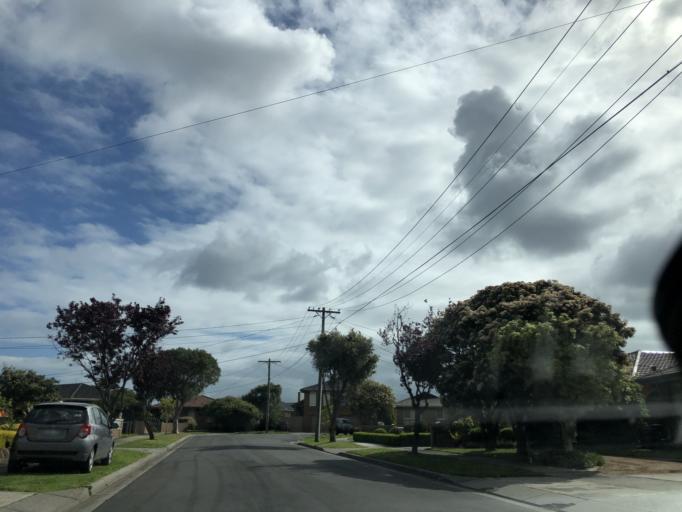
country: AU
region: Victoria
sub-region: Kingston
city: Clayton South
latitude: -37.9387
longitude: 145.1105
